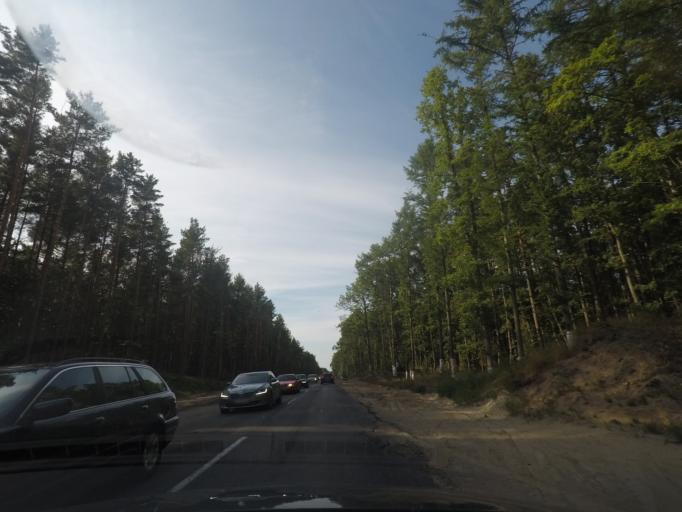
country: PL
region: Pomeranian Voivodeship
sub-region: Powiat leborski
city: Leba
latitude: 54.7074
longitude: 17.5824
